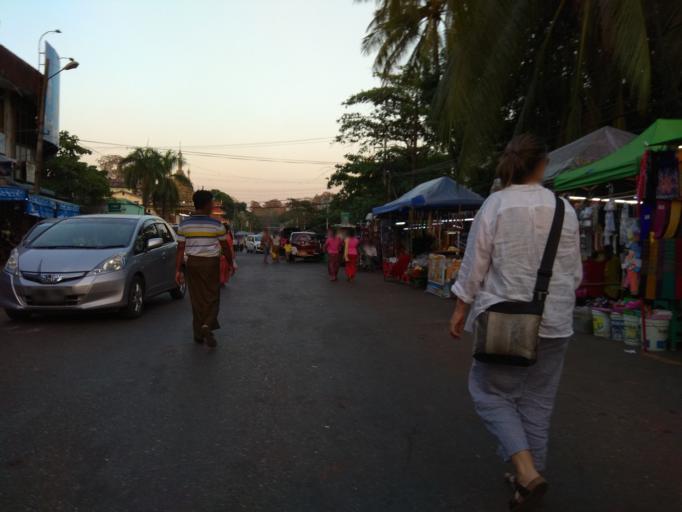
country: MM
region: Yangon
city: Yangon
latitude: 16.7992
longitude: 96.1539
